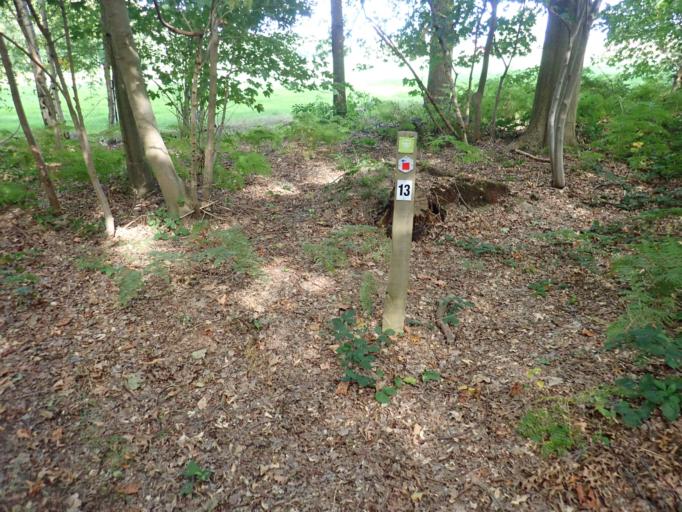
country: BE
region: Flanders
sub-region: Provincie Antwerpen
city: Lint
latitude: 51.1429
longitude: 4.5024
